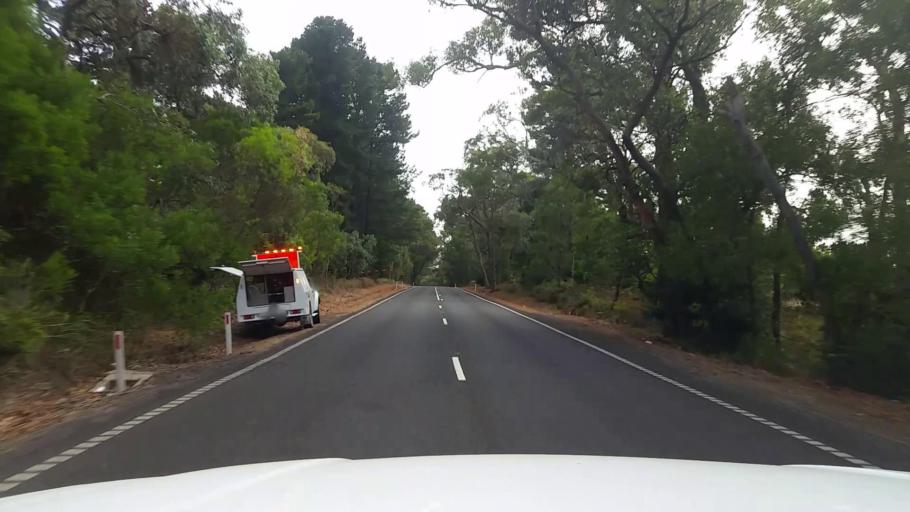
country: AU
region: Victoria
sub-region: Mornington Peninsula
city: Balnarring
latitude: -38.3284
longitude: 145.0935
